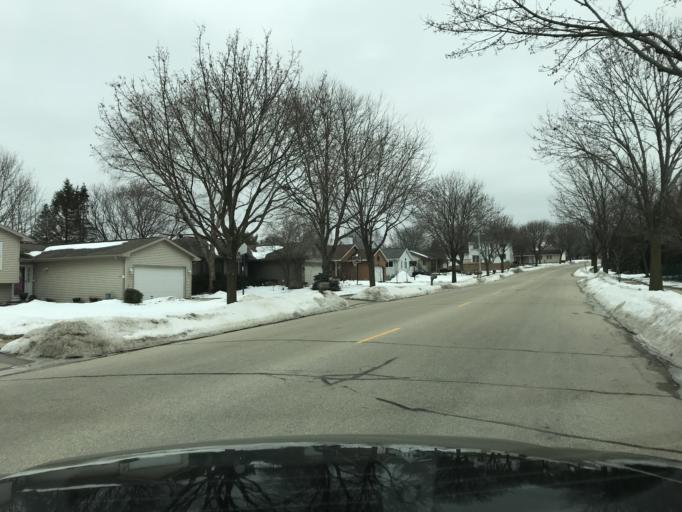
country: US
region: Wisconsin
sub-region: Dane County
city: Monona
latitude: 43.0752
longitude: -89.2829
